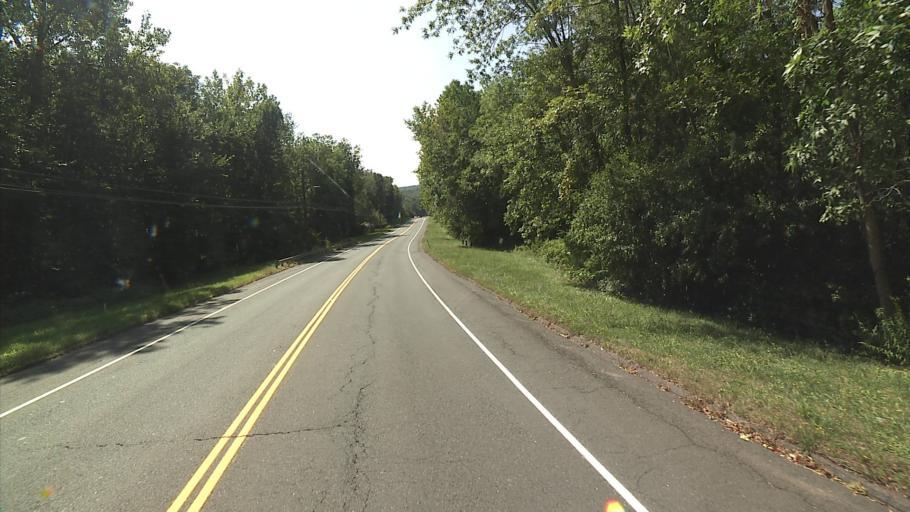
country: US
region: Connecticut
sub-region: Hartford County
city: Blue Hills
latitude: 41.8293
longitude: -72.7612
